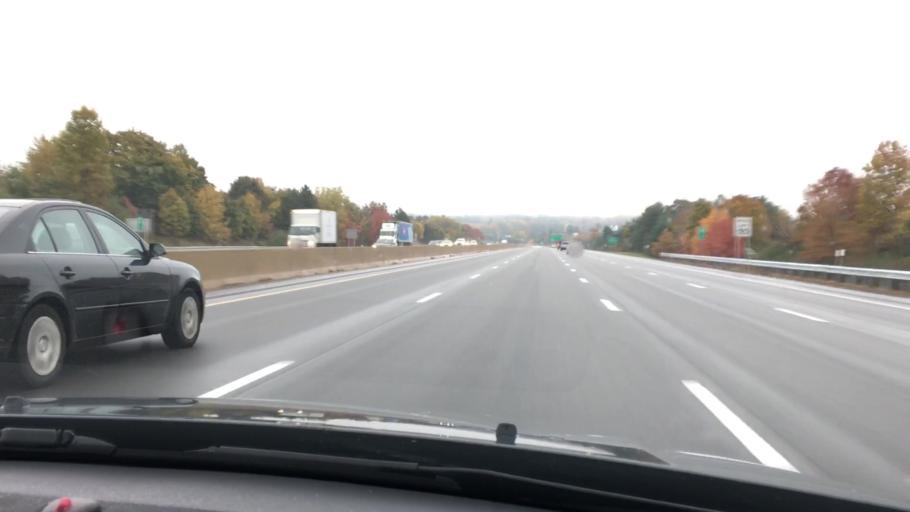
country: US
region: New Hampshire
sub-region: Hillsborough County
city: Nashua
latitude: 42.7374
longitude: -71.4810
